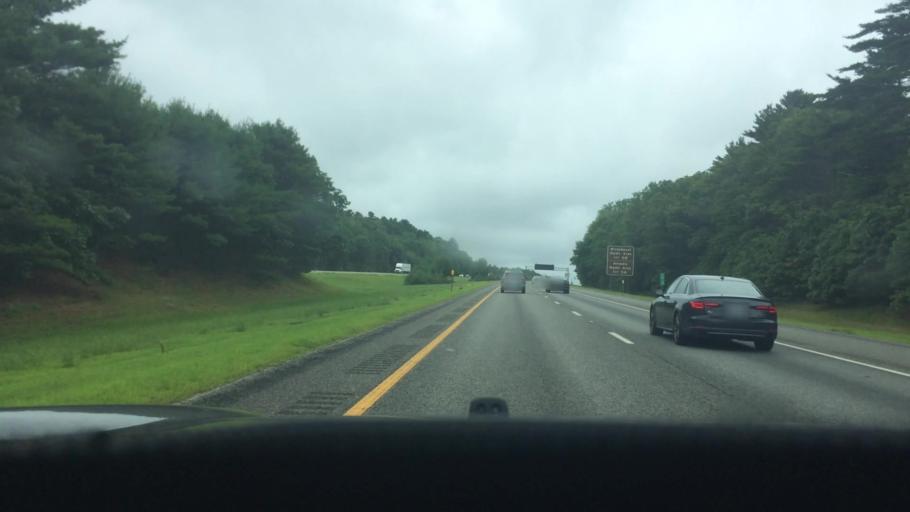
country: US
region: Rhode Island
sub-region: Kent County
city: West Greenwich
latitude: 41.6247
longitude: -71.6409
